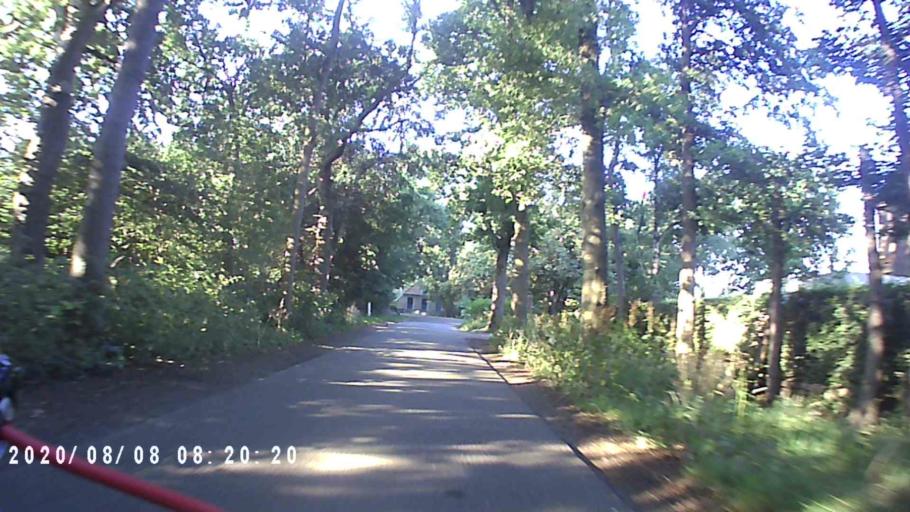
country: NL
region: Groningen
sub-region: Gemeente Leek
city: Leek
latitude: 53.0937
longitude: 6.3142
